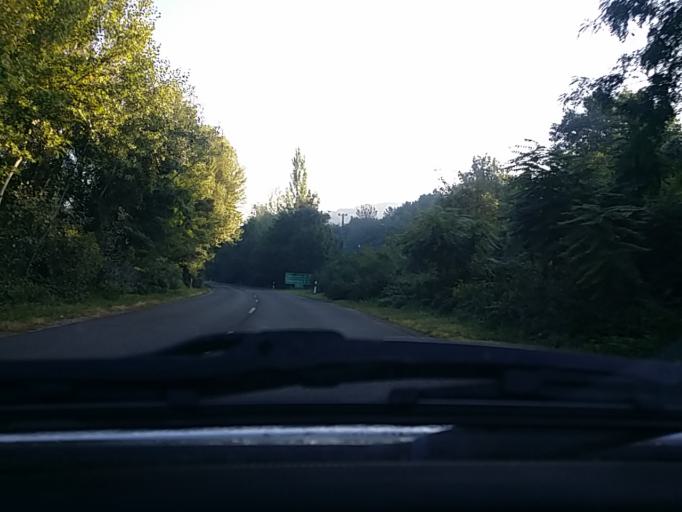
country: HU
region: Pest
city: Visegrad
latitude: 47.7623
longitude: 18.9493
